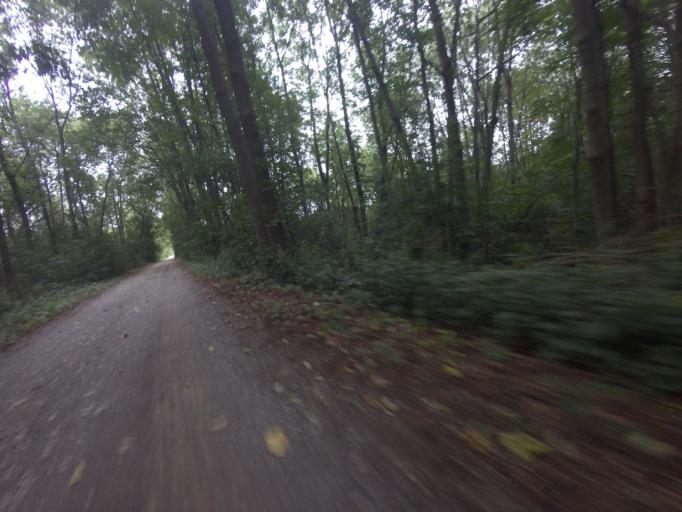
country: CA
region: Ontario
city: Omemee
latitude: 44.3910
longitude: -78.7572
